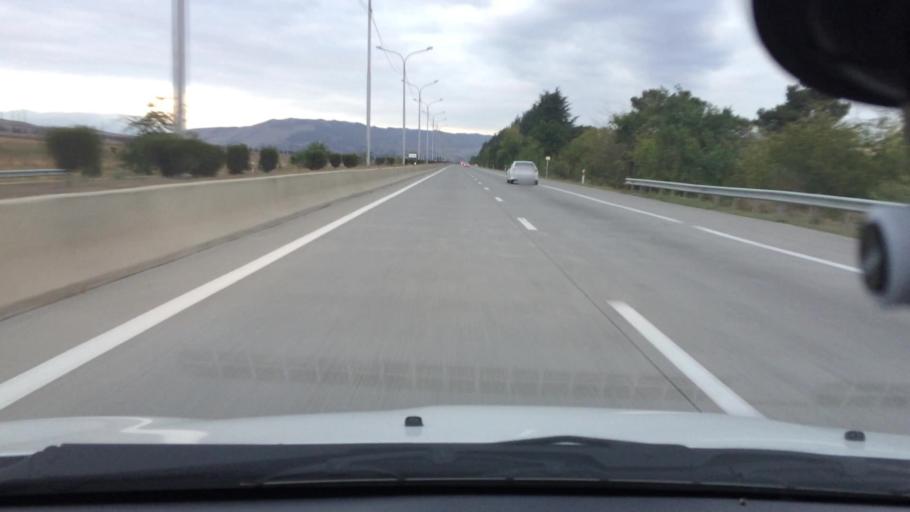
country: GE
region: Mtskheta-Mtianeti
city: Mtskheta
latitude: 41.8968
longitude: 44.6190
